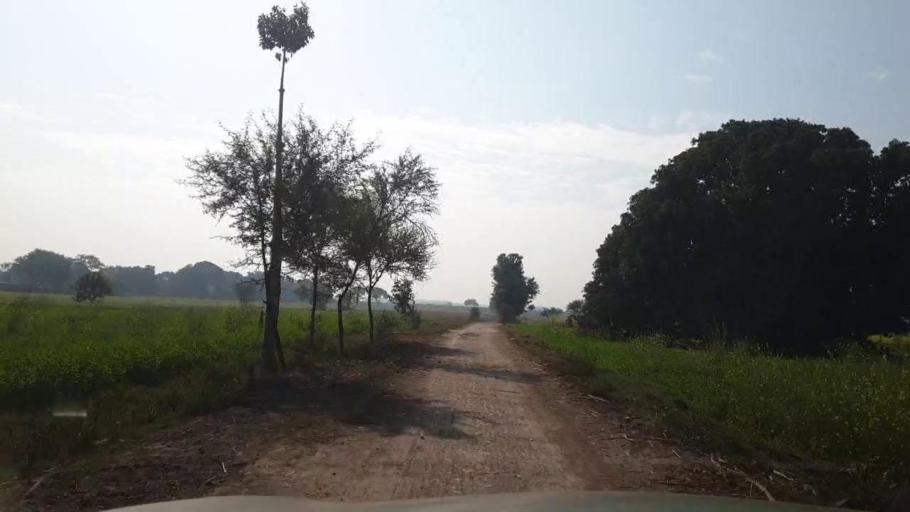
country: PK
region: Sindh
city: Tando Allahyar
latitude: 25.4680
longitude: 68.6334
